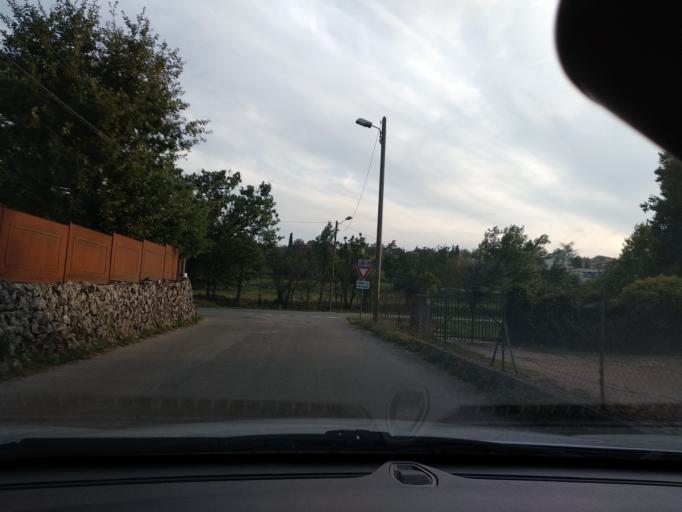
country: FR
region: Provence-Alpes-Cote d'Azur
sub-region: Departement des Alpes-Maritimes
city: Saint-Cezaire-sur-Siagne
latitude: 43.6518
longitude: 6.7991
